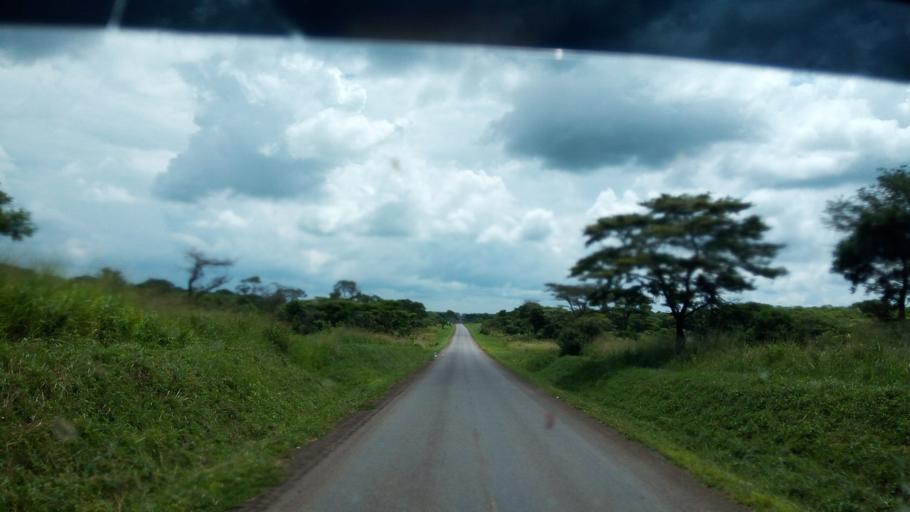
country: UG
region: Northern Region
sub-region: Oyam District
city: Oyam
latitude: 2.3338
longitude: 32.1293
